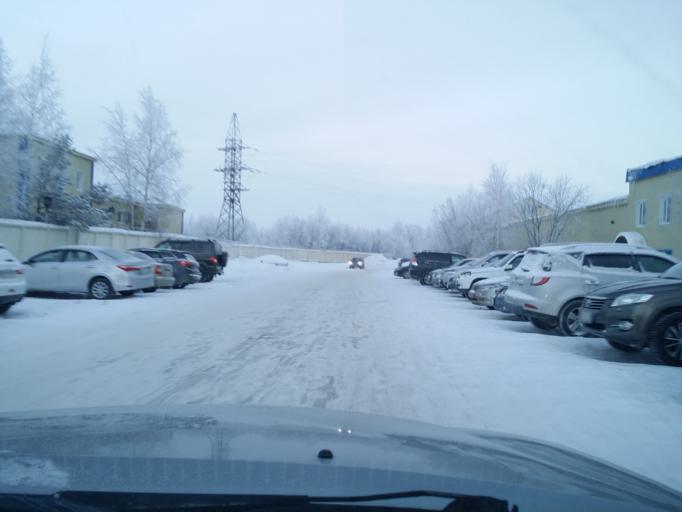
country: RU
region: Khanty-Mansiyskiy Avtonomnyy Okrug
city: Nizhnevartovsk
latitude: 60.9522
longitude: 76.5003
